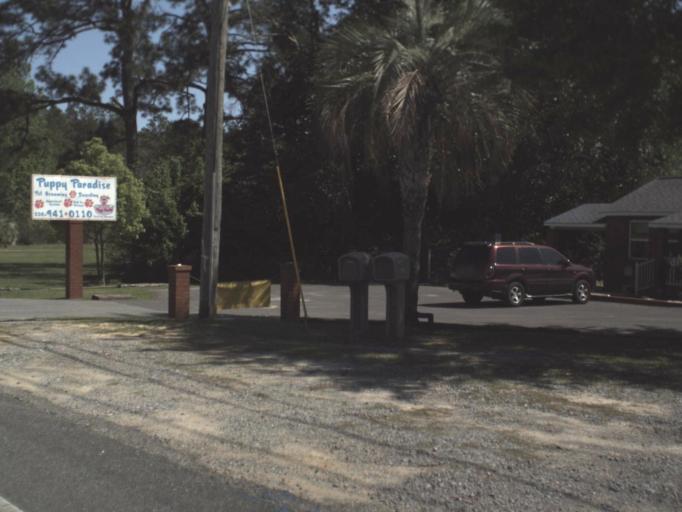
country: US
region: Florida
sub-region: Escambia County
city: Bellview
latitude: 30.4943
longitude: -87.3264
